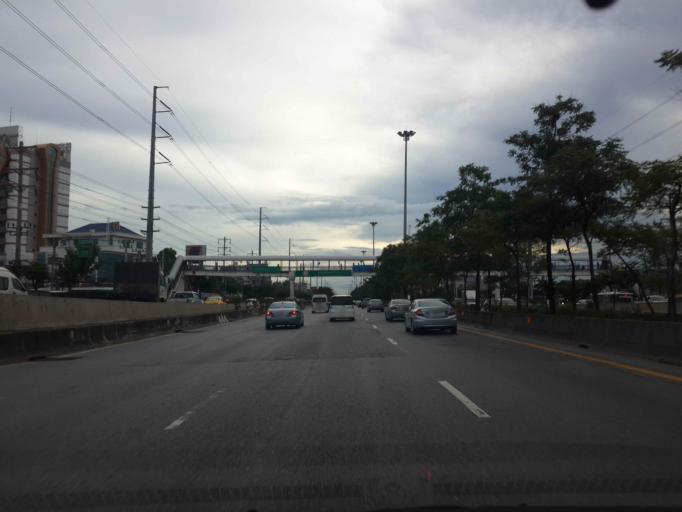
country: TH
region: Bangkok
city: Bang Khun Thian
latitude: 13.6732
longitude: 100.4574
